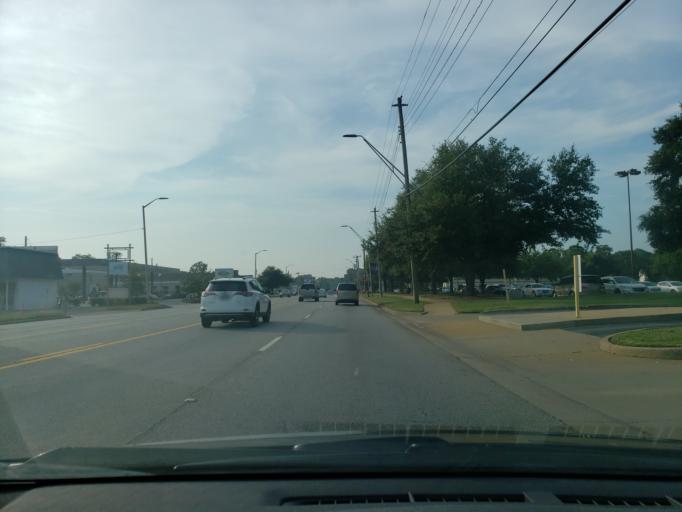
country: US
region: Georgia
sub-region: Dougherty County
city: Albany
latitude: 31.6051
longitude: -84.2061
